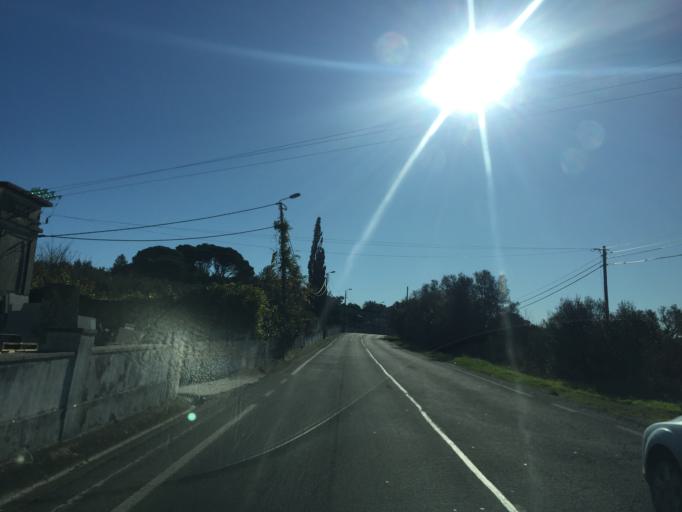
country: PT
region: Lisbon
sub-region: Sintra
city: Pero Pinheiro
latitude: 38.8373
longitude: -9.3107
